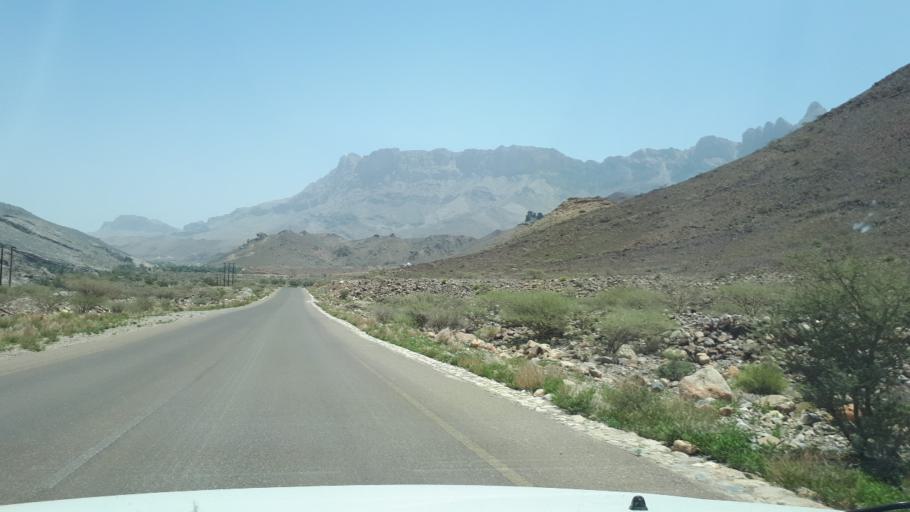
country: OM
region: Muhafazat ad Dakhiliyah
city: Bahla'
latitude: 23.1808
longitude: 57.1418
